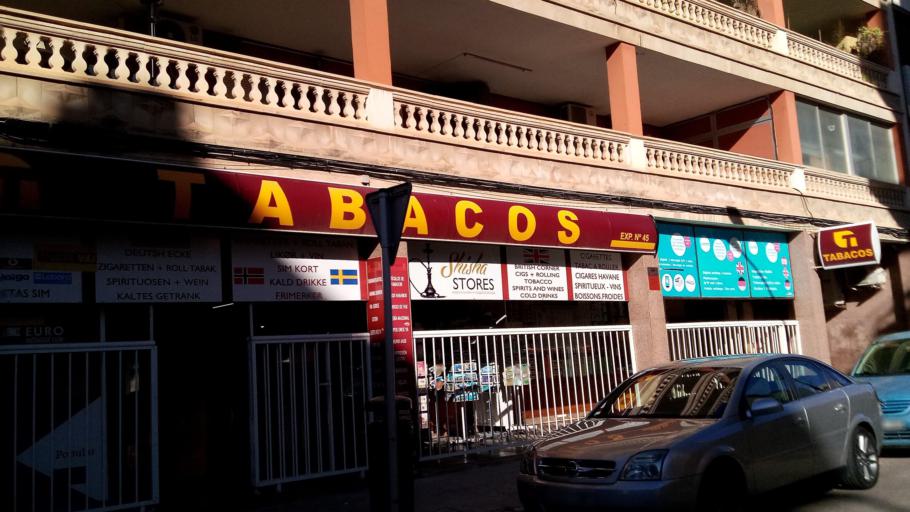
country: ES
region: Balearic Islands
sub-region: Illes Balears
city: s'Arenal
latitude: 39.5364
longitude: 2.7183
